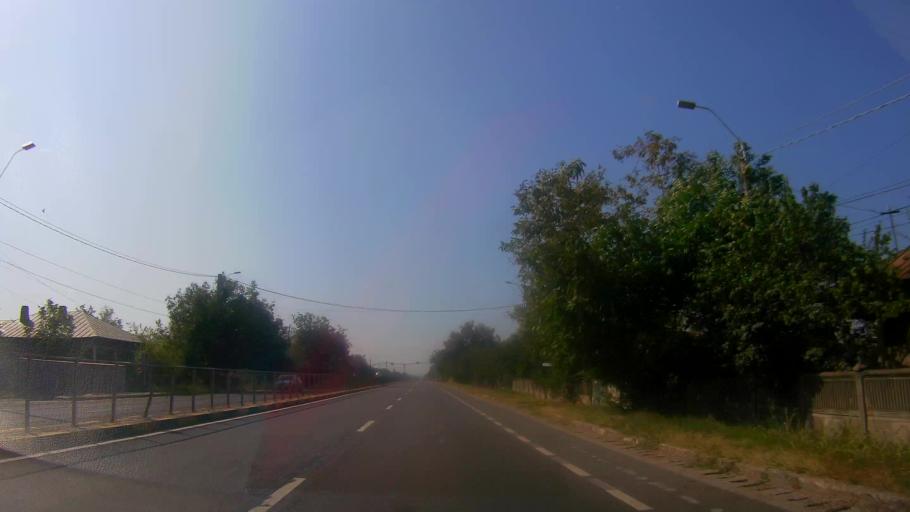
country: RO
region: Giurgiu
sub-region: Comuna Daia
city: Daia
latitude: 43.9862
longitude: 25.9899
